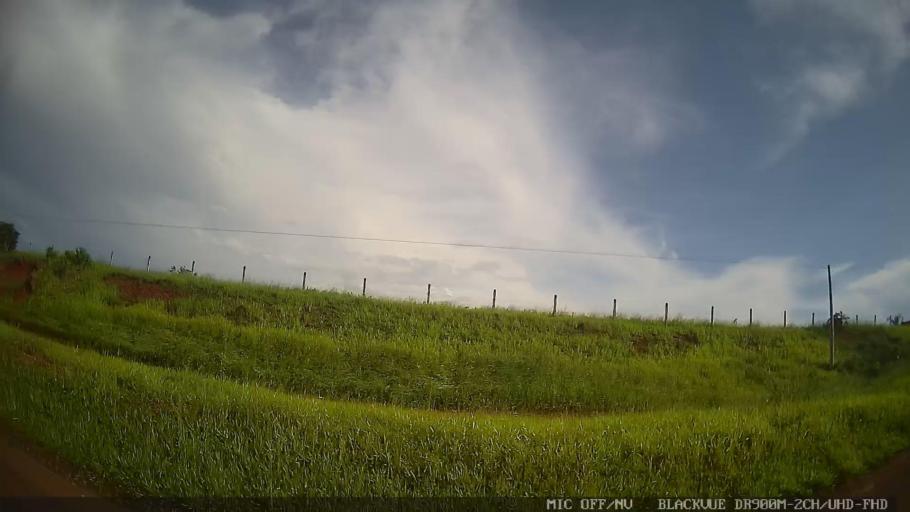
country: BR
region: Sao Paulo
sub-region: Tiete
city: Tiete
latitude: -23.0867
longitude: -47.6791
